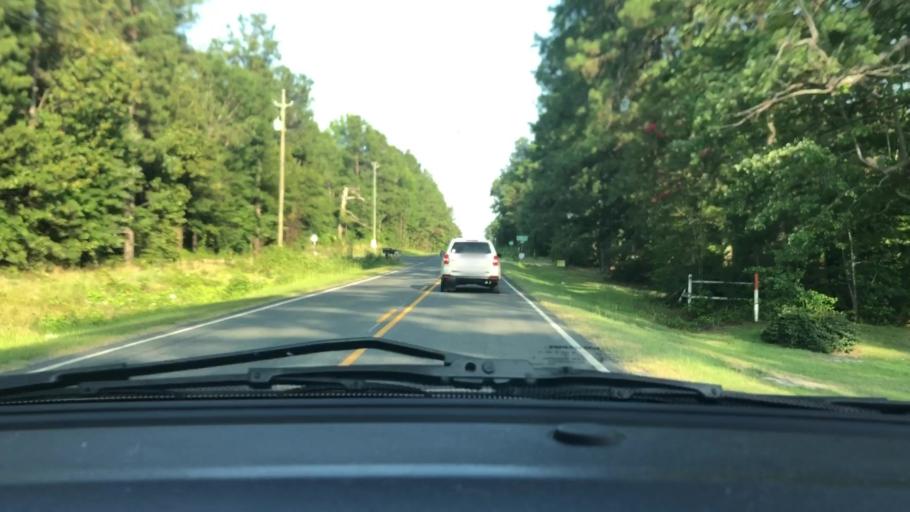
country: US
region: North Carolina
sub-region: Lee County
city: Broadway
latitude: 35.3611
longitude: -79.0867
